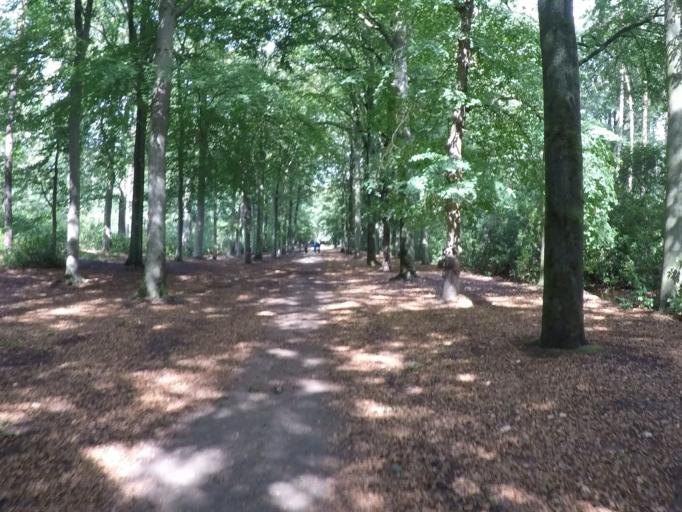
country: BE
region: Flanders
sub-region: Provincie Antwerpen
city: Vorselaar
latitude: 51.2100
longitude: 4.7765
